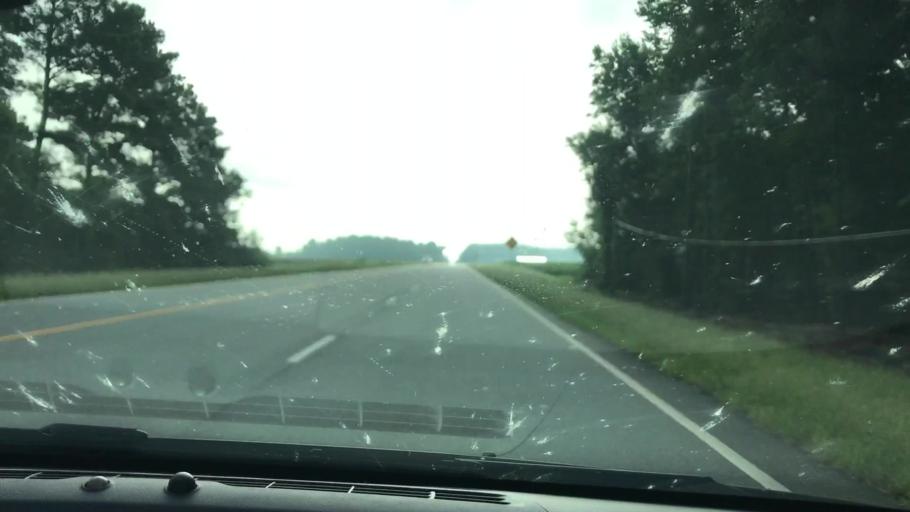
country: US
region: Georgia
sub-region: Randolph County
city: Shellman
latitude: 31.7706
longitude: -84.5440
